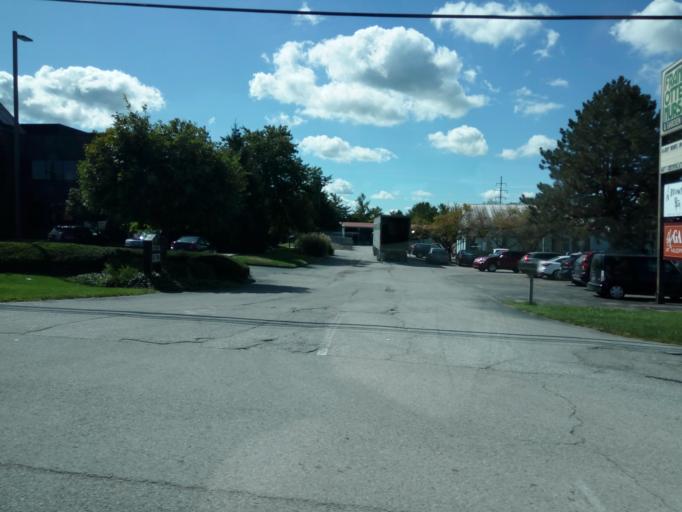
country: US
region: Kentucky
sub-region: Jefferson County
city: Middletown
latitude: 38.2431
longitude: -85.5160
